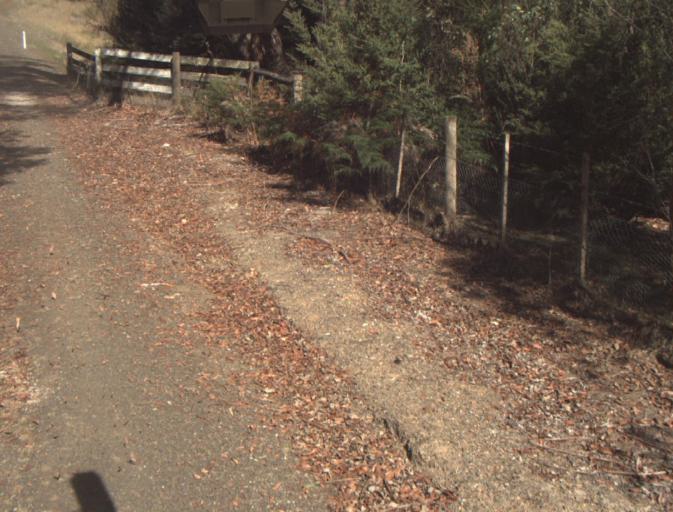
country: AU
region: Tasmania
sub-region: Launceston
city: Newstead
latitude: -41.3051
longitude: 147.3138
